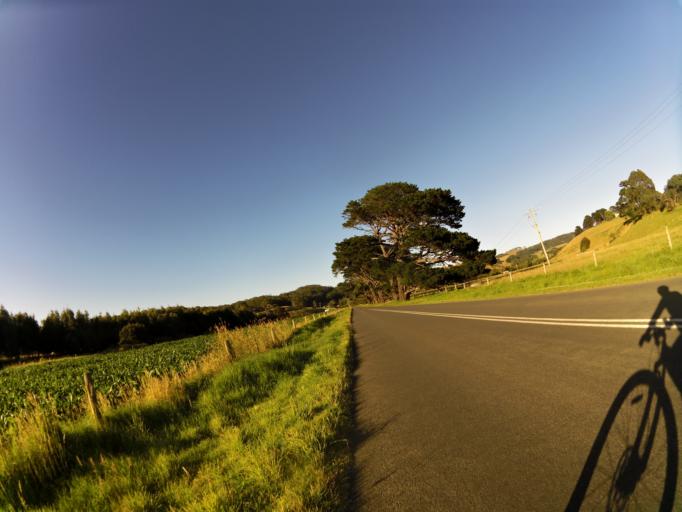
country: AU
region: Victoria
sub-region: Colac-Otway
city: Apollo Bay
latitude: -38.7678
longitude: 143.6523
